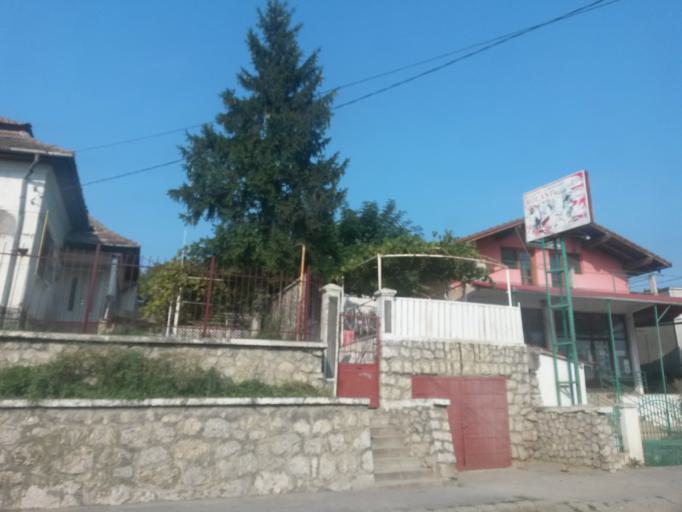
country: RO
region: Cluj
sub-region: Comuna Sandulesti
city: Copaceni
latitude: 46.5842
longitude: 23.7626
